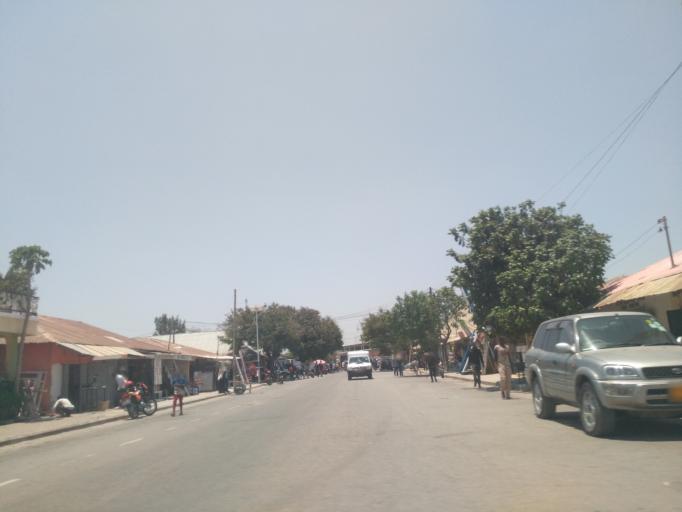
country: TZ
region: Dodoma
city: Dodoma
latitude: -6.1752
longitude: 35.7440
